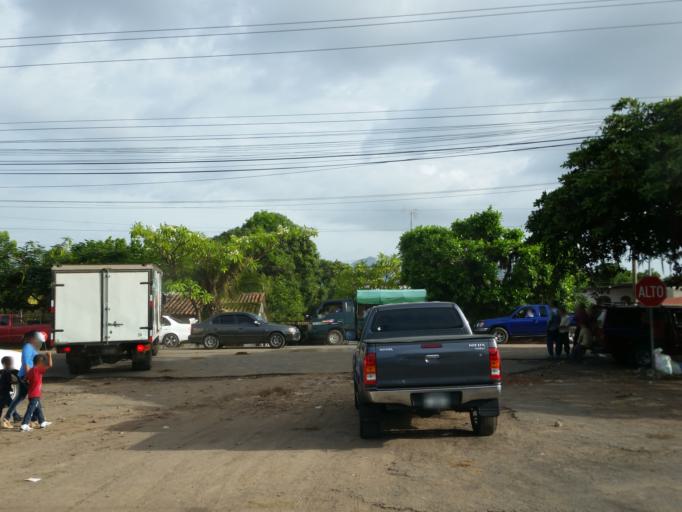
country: NI
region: Granada
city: Granada
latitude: 11.9366
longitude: -85.9643
